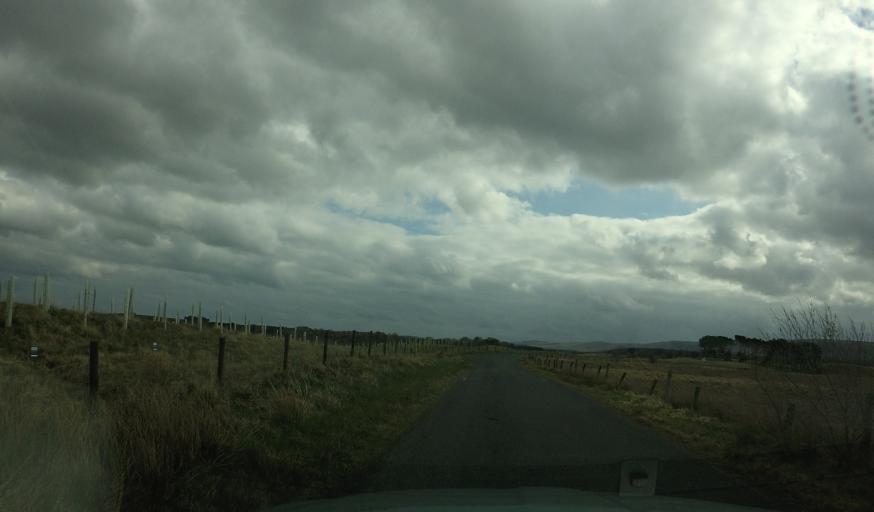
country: GB
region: Scotland
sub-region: Midlothian
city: Penicuik
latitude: 55.7614
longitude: -3.1592
